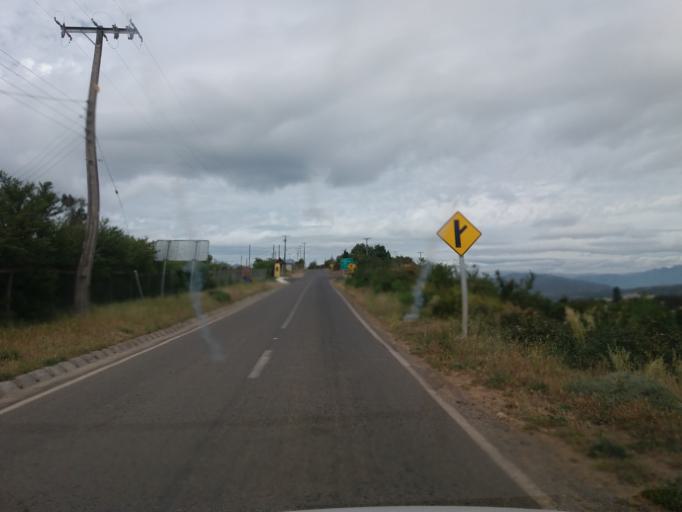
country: CL
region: Valparaiso
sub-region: Provincia de Quillota
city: Quillota
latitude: -32.9175
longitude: -71.3475
